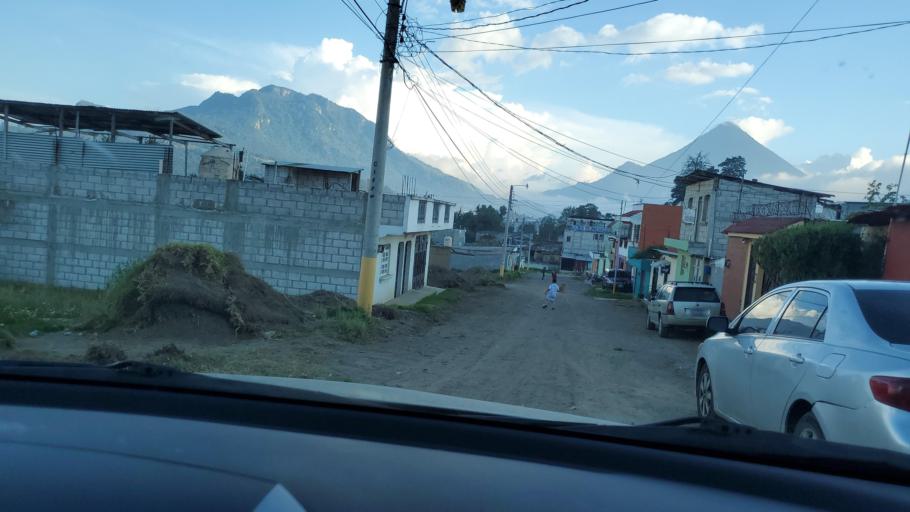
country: GT
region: Quetzaltenango
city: Quetzaltenango
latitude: 14.8403
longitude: -91.5431
